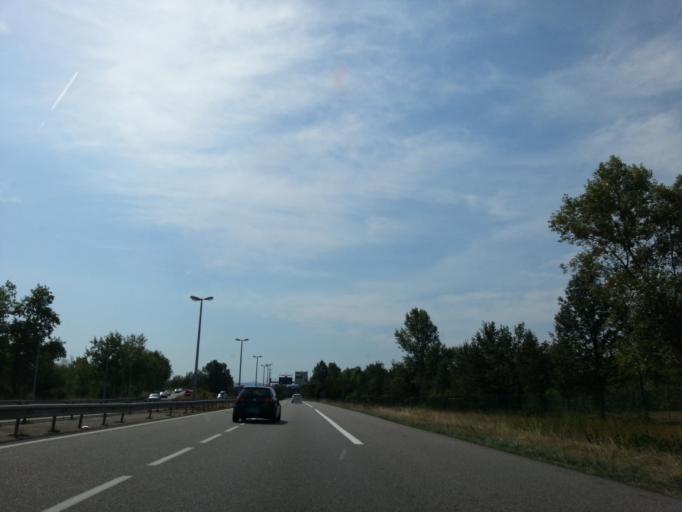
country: FR
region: Alsace
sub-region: Departement du Haut-Rhin
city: Saint-Louis
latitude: 47.5919
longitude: 7.5447
